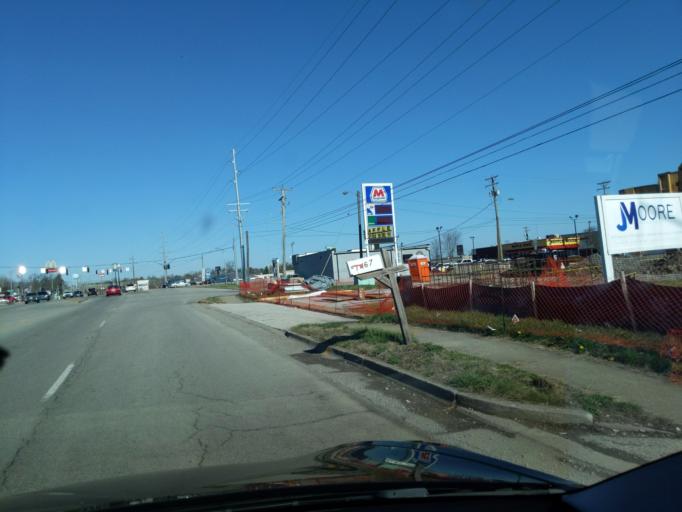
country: US
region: Kentucky
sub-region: Clark County
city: Winchester
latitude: 38.0064
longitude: -84.2092
